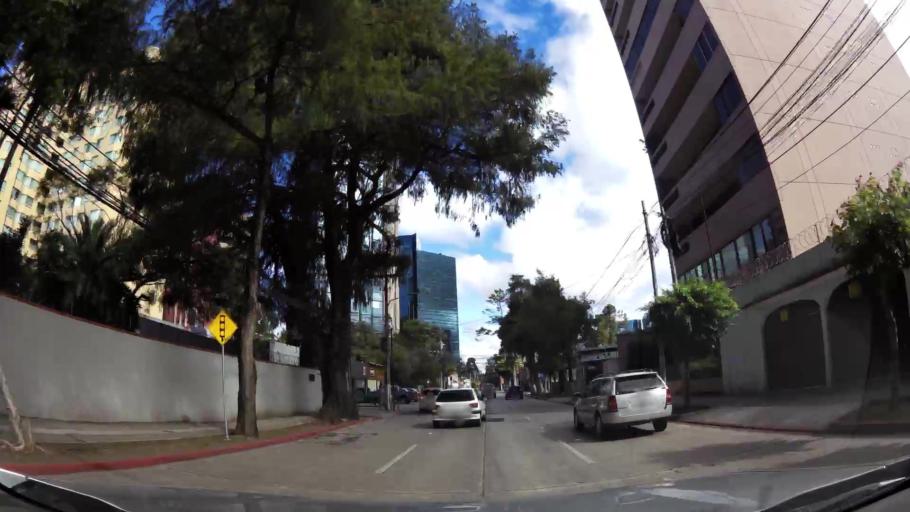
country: GT
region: Guatemala
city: Santa Catarina Pinula
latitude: 14.5971
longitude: -90.5132
